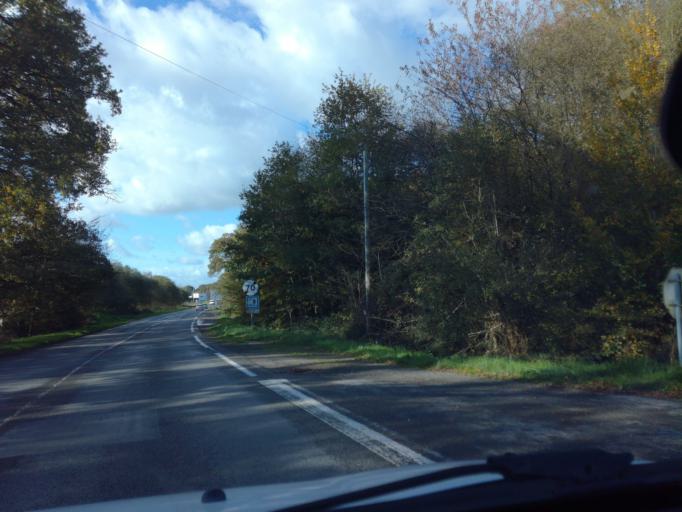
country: FR
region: Brittany
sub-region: Departement d'Ille-et-Vilaine
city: Mordelles
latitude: 48.0688
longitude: -1.8264
